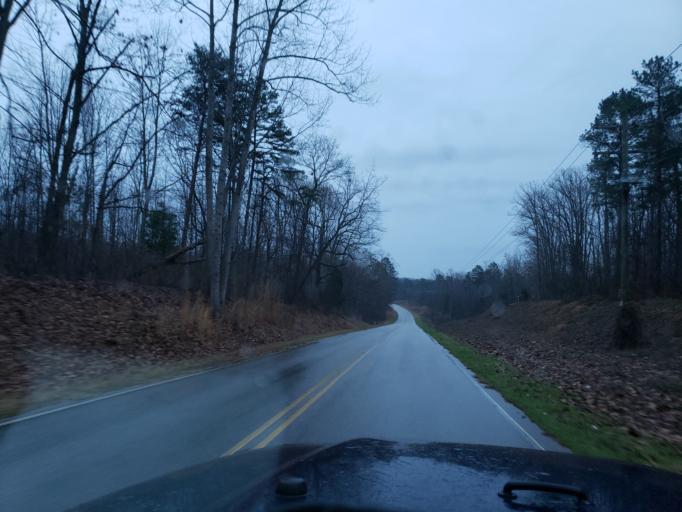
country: US
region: South Carolina
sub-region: Cherokee County
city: Blacksburg
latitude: 35.1580
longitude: -81.4629
